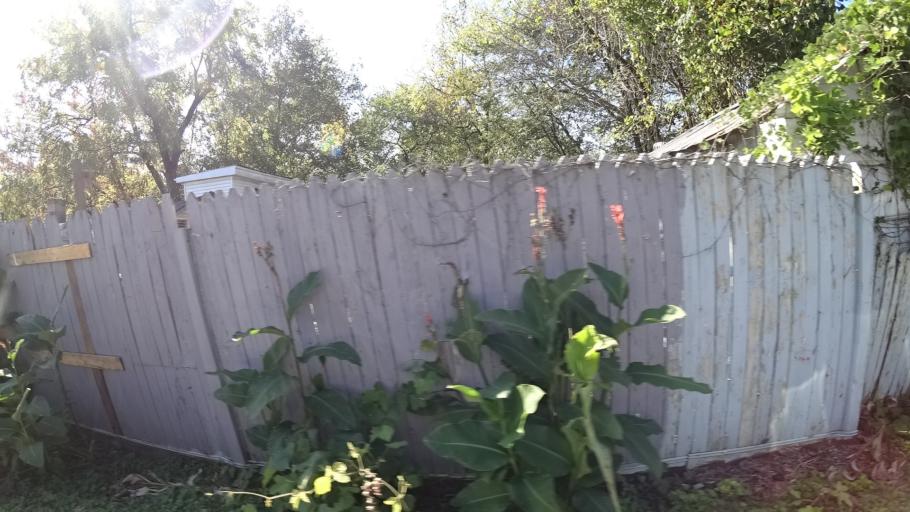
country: US
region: Tennessee
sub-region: Knox County
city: Knoxville
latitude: 35.9533
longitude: -83.9704
